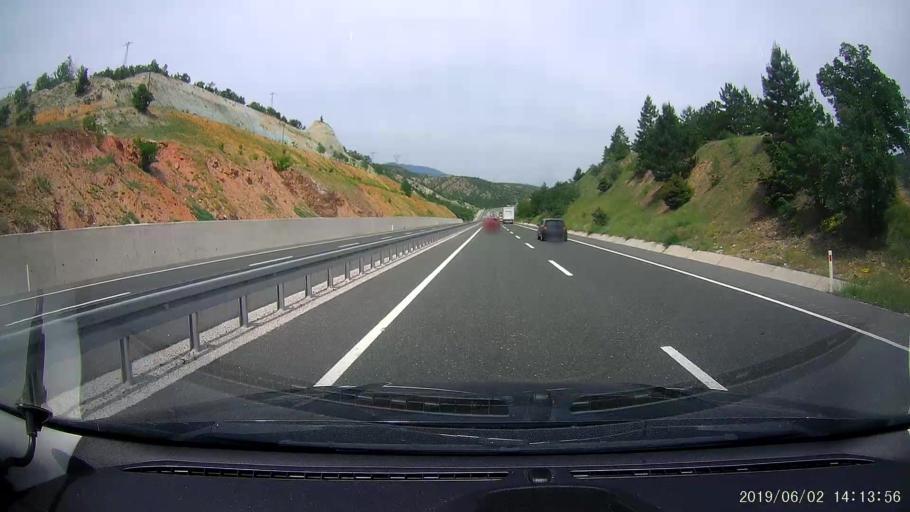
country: TR
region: Cankiri
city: Yaprakli
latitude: 40.9299
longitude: 33.8425
